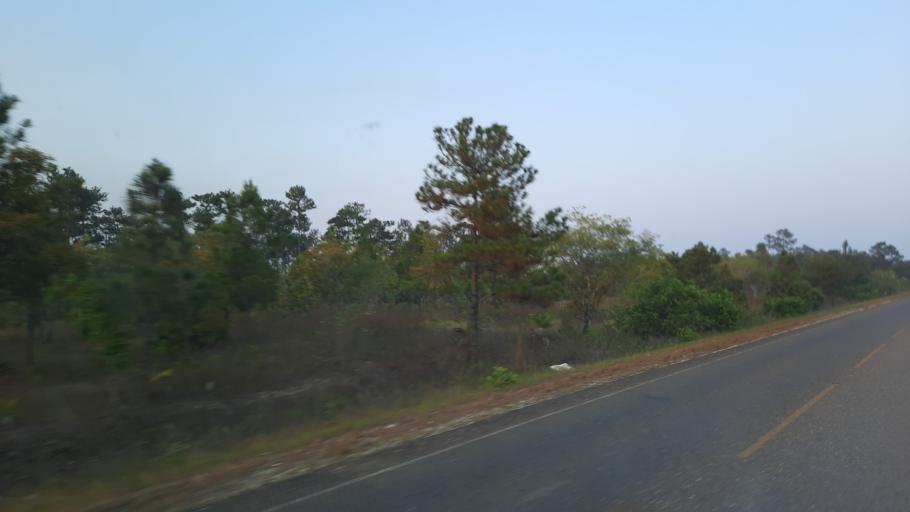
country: BZ
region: Stann Creek
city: Placencia
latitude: 16.5311
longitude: -88.4531
